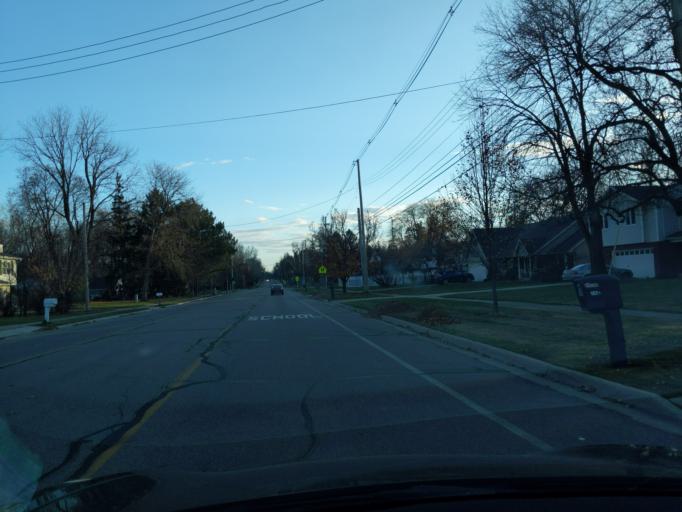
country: US
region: Michigan
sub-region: Ingham County
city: East Lansing
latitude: 42.7546
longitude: -84.4935
